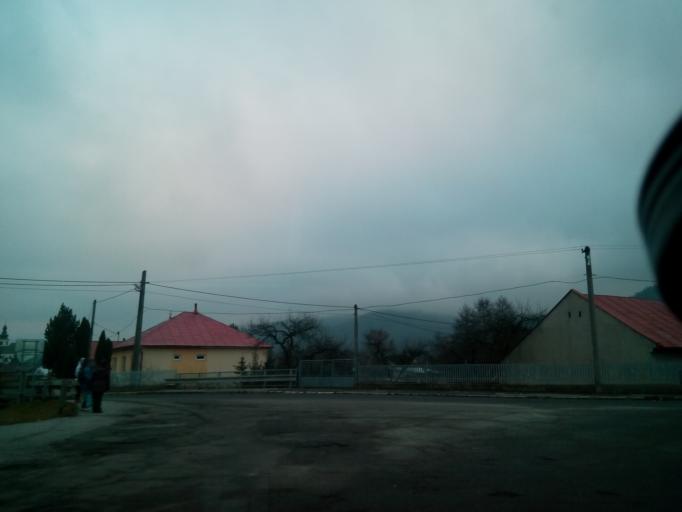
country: SK
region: Kosicky
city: Krompachy
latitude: 48.9238
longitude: 20.9327
